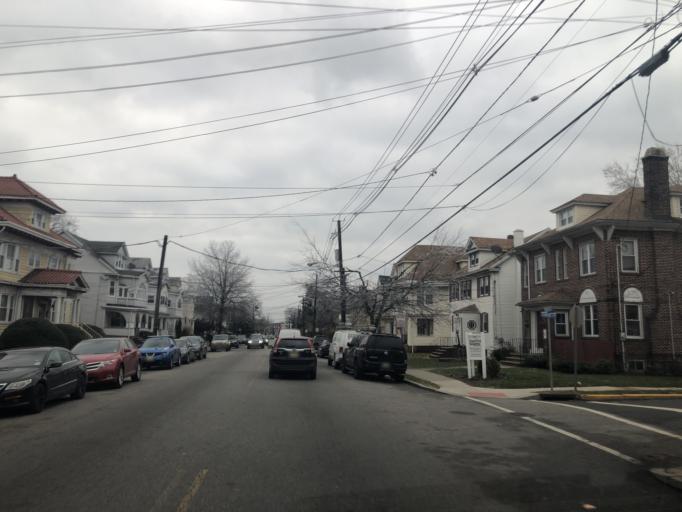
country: US
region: New Jersey
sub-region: Essex County
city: Irvington
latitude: 40.7289
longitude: -74.2405
